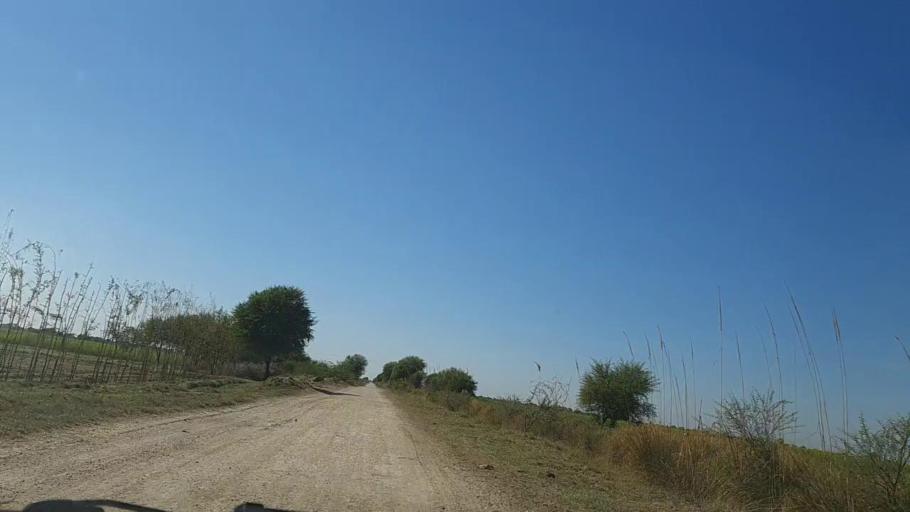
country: PK
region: Sindh
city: Pithoro
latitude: 25.5614
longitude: 69.4666
